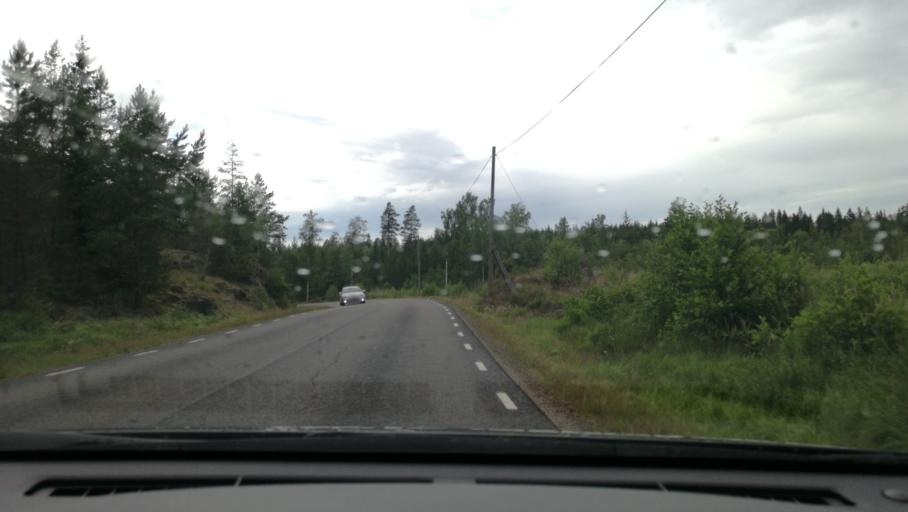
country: SE
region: OEstergoetland
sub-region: Norrkopings Kommun
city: Jursla
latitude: 58.8044
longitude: 16.1274
